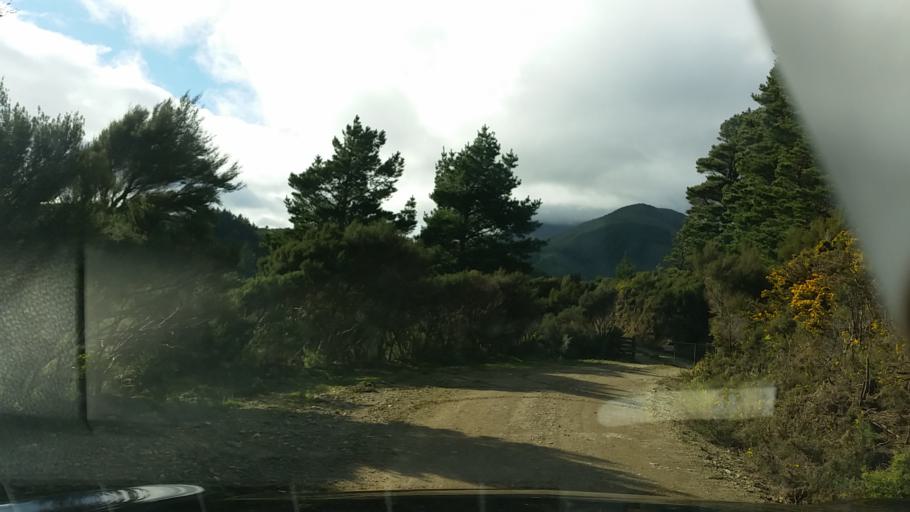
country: NZ
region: Marlborough
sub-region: Marlborough District
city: Picton
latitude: -40.9711
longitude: 173.8948
